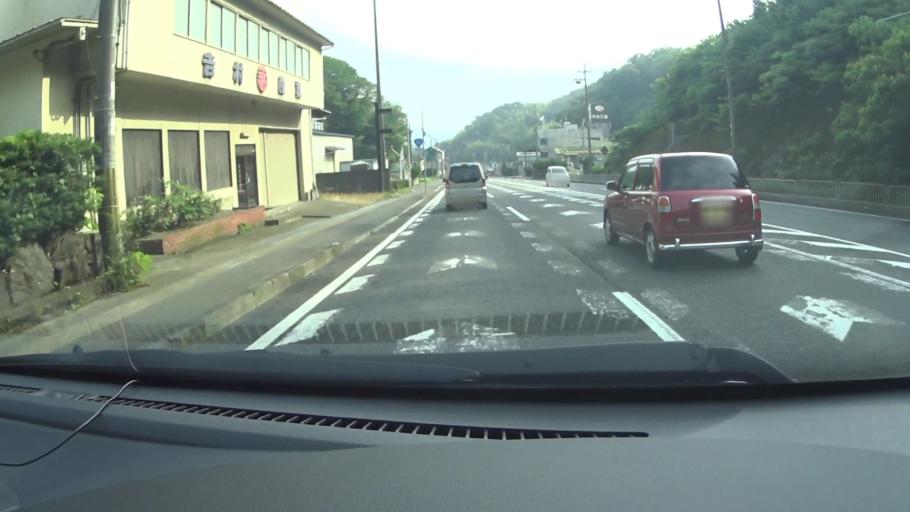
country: JP
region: Kyoto
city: Maizuru
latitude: 35.4587
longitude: 135.3529
